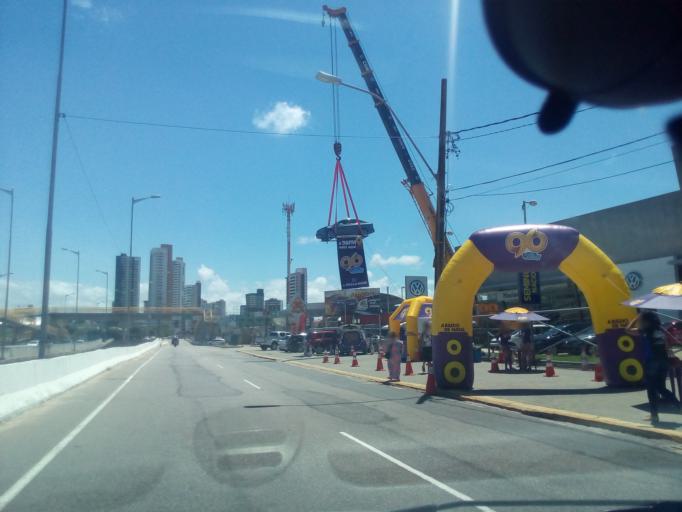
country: BR
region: Rio Grande do Norte
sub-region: Natal
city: Natal
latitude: -5.8249
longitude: -35.2153
